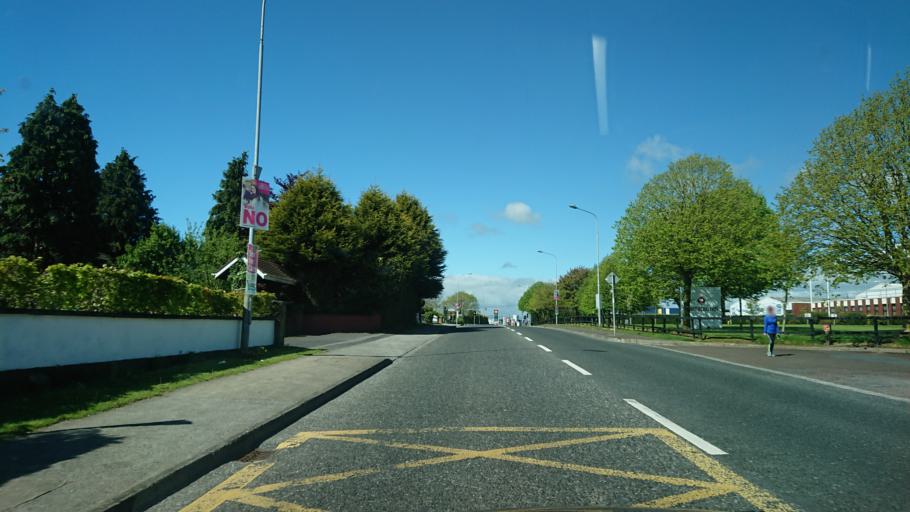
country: IE
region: Munster
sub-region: Waterford
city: Waterford
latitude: 52.2433
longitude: -7.1526
